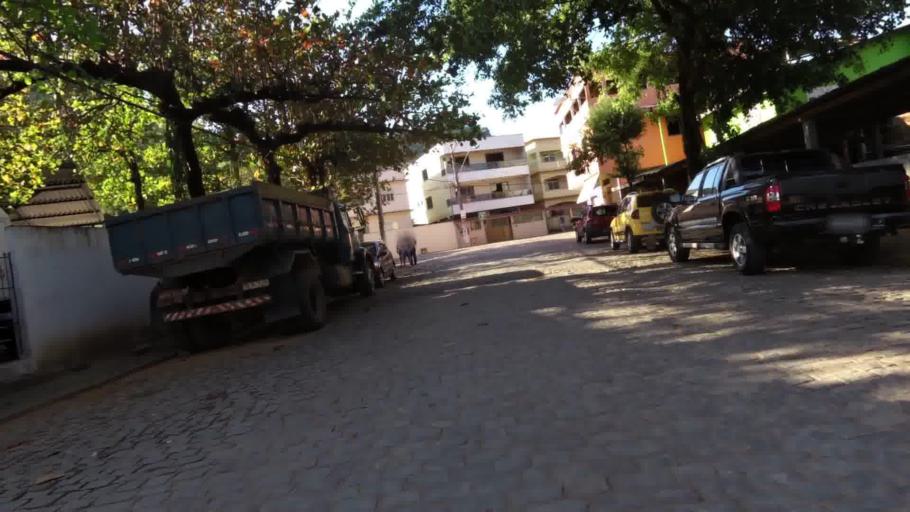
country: BR
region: Espirito Santo
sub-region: Alfredo Chaves
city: Alfredo Chaves
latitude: -20.6338
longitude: -40.7486
